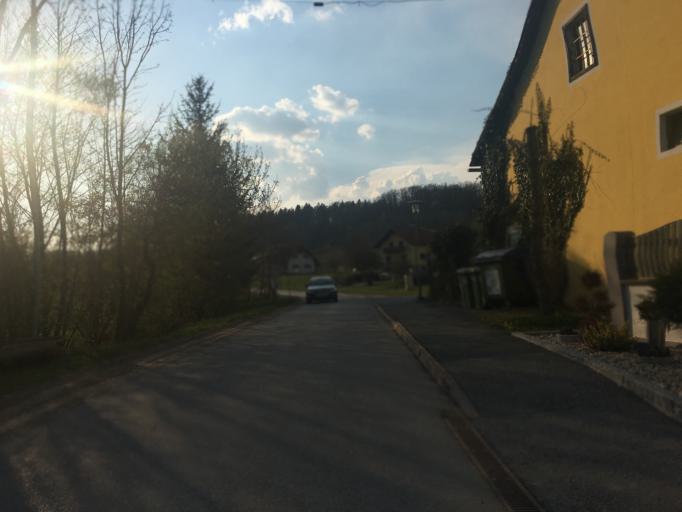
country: AT
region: Styria
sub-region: Politischer Bezirk Graz-Umgebung
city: Nestelbach bei Graz
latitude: 47.0835
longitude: 15.6213
